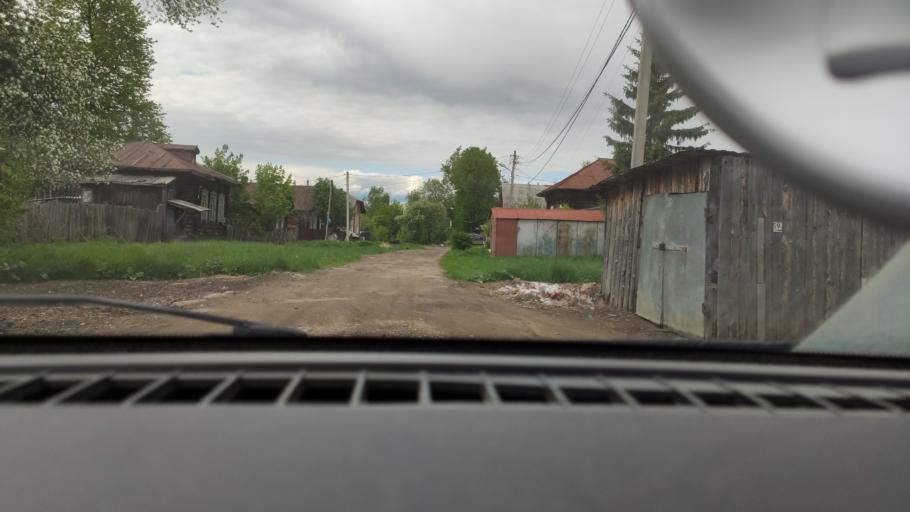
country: RU
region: Perm
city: Perm
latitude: 58.0201
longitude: 56.3274
